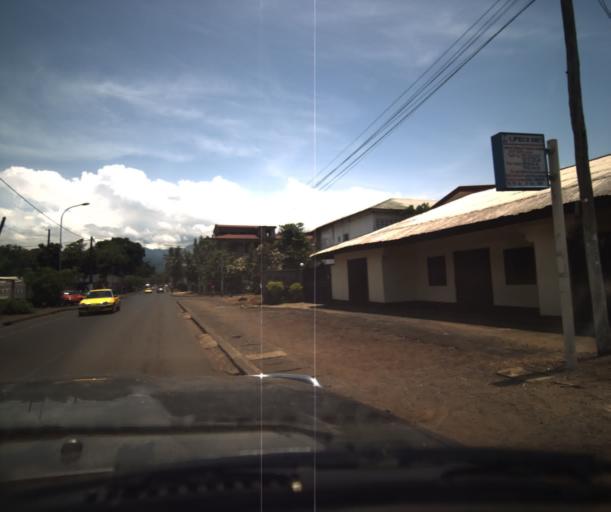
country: CM
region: South-West Province
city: Limbe
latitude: 4.0075
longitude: 9.2098
